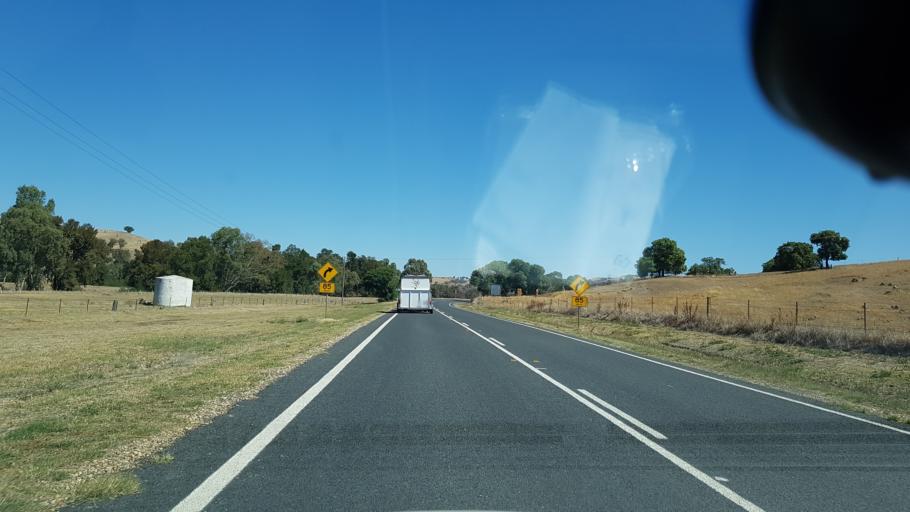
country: AU
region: New South Wales
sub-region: Gundagai
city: Gundagai
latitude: -34.8220
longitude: 148.3493
